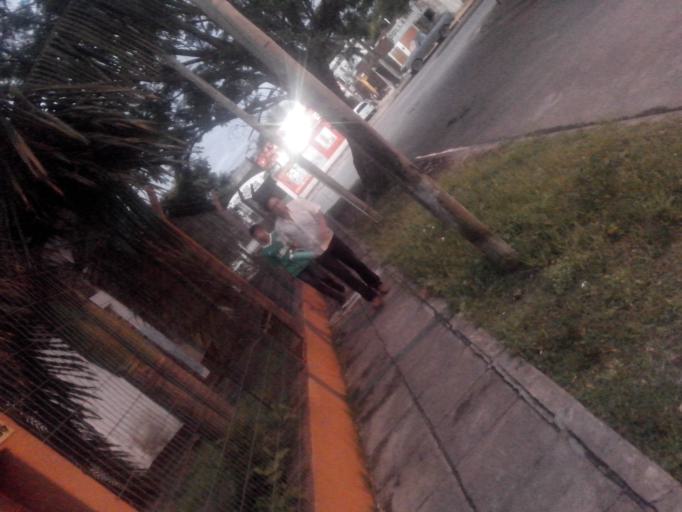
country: AR
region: Corrientes
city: Corrientes
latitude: -27.4850
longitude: -58.8450
